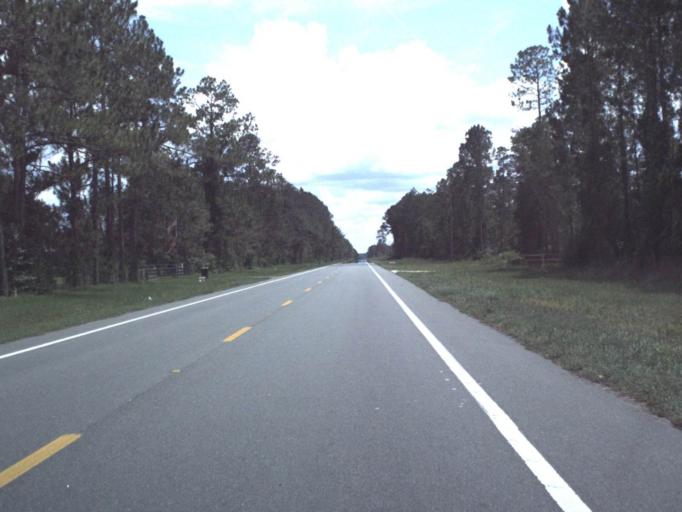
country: US
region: Florida
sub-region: Columbia County
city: Five Points
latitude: 30.3975
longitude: -82.6309
